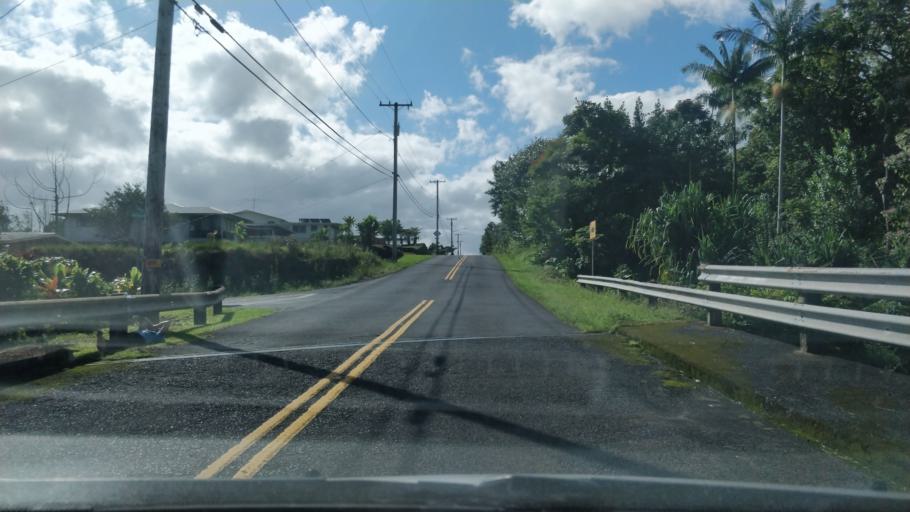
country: US
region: Hawaii
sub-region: Hawaii County
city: Hilo
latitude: 19.6755
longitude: -155.1060
